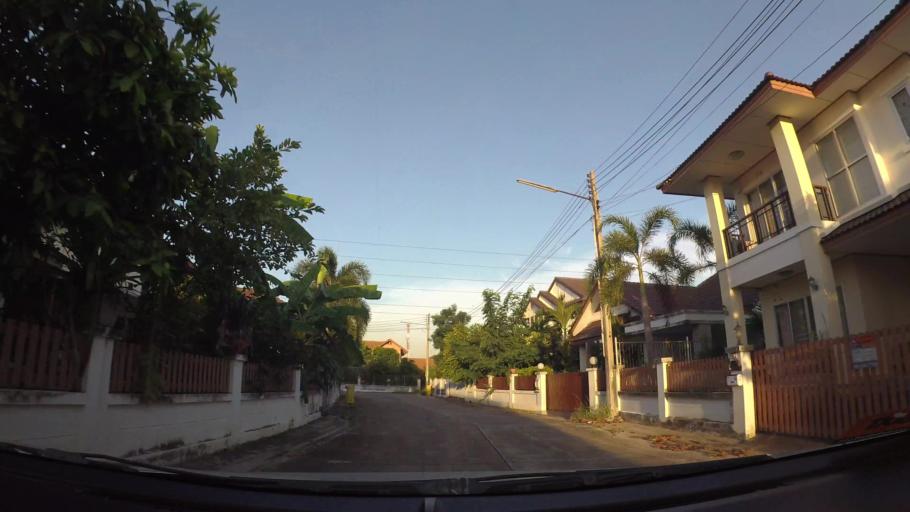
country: TH
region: Chon Buri
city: Si Racha
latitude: 13.1282
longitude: 100.9395
